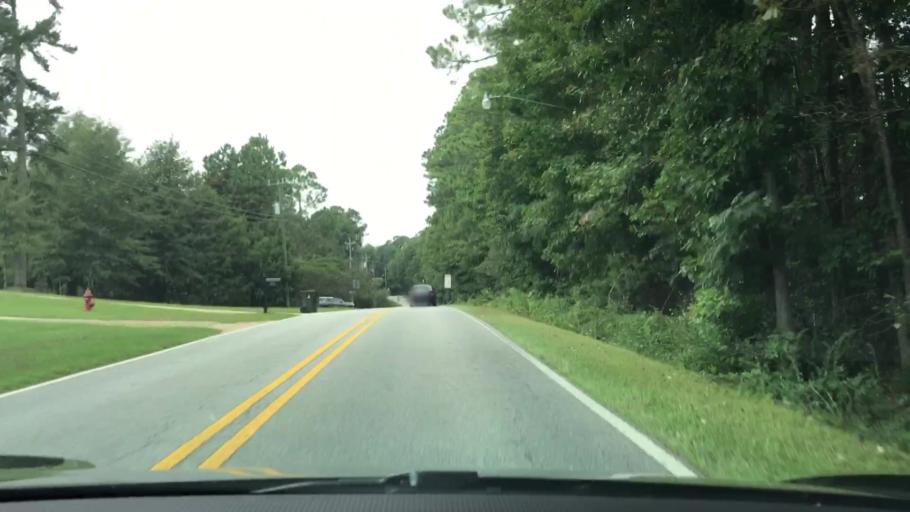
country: US
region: Alabama
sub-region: Lee County
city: Auburn
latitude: 32.6184
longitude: -85.4428
